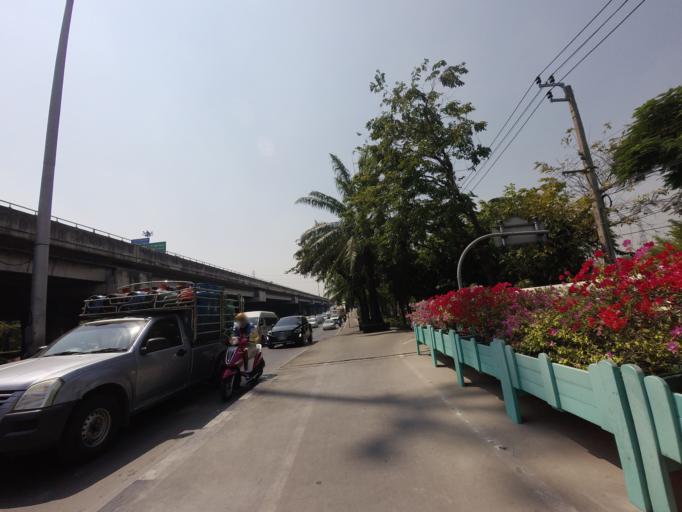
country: TH
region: Bangkok
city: Huai Khwang
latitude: 13.7617
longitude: 100.5975
